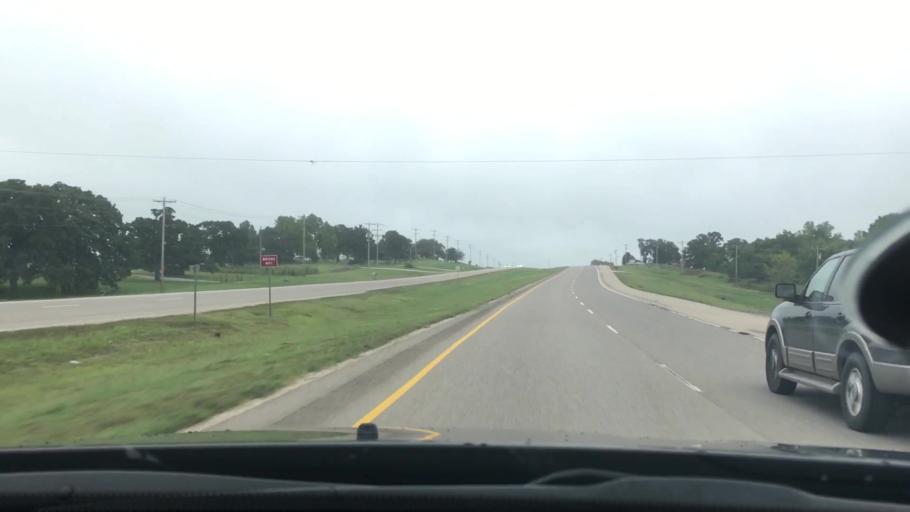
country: US
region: Oklahoma
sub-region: Seminole County
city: Seminole
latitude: 35.3115
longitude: -96.6714
